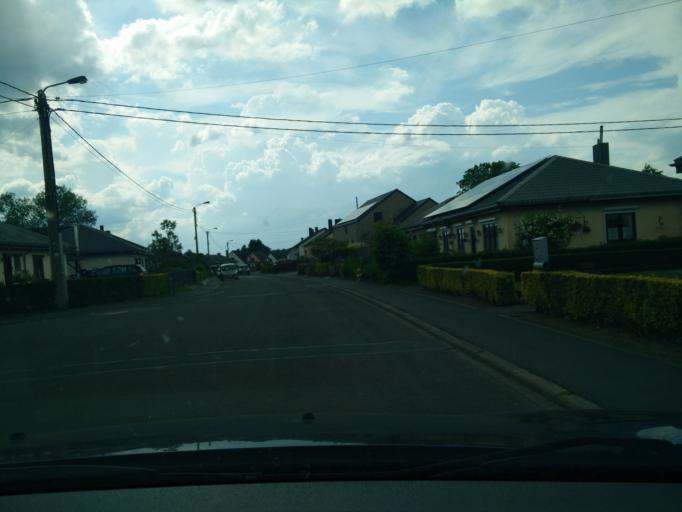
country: BE
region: Wallonia
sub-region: Province de Namur
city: Philippeville
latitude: 50.1904
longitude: 4.5513
